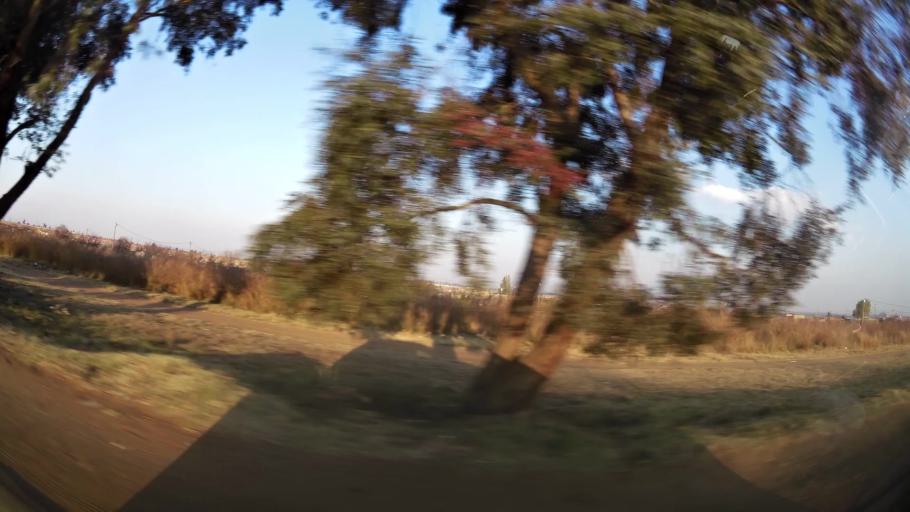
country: ZA
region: Gauteng
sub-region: Ekurhuleni Metropolitan Municipality
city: Benoni
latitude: -26.1514
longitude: 28.3811
